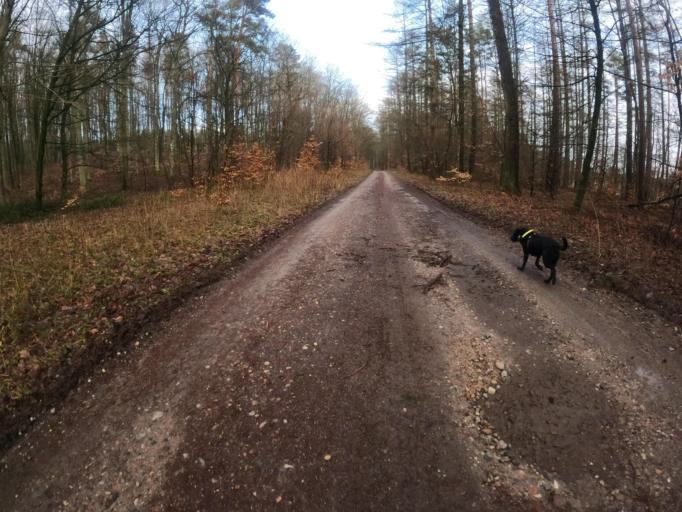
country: PL
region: West Pomeranian Voivodeship
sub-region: Powiat slawienski
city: Slawno
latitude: 54.2557
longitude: 16.6862
